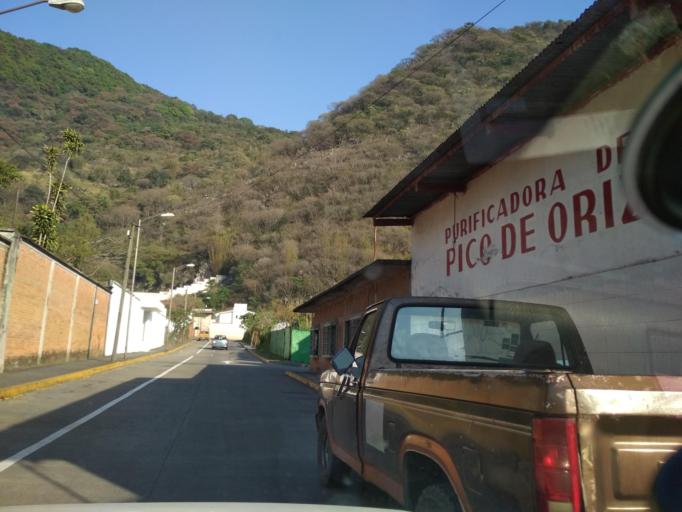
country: MX
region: Veracruz
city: Ixtac Zoquitlan
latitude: 18.8607
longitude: -97.0792
